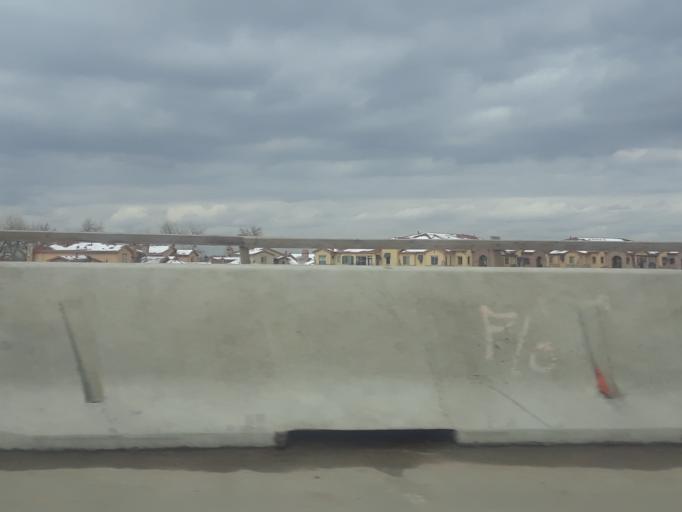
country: US
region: Colorado
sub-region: Arapahoe County
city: Columbine Valley
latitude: 39.5632
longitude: -105.0181
